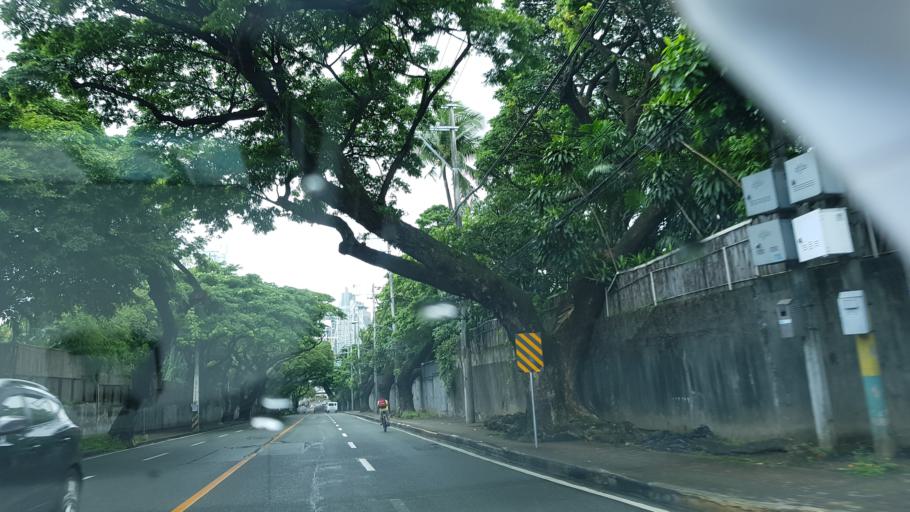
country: PH
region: Metro Manila
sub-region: Makati City
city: Makati City
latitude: 14.5484
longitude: 121.0327
